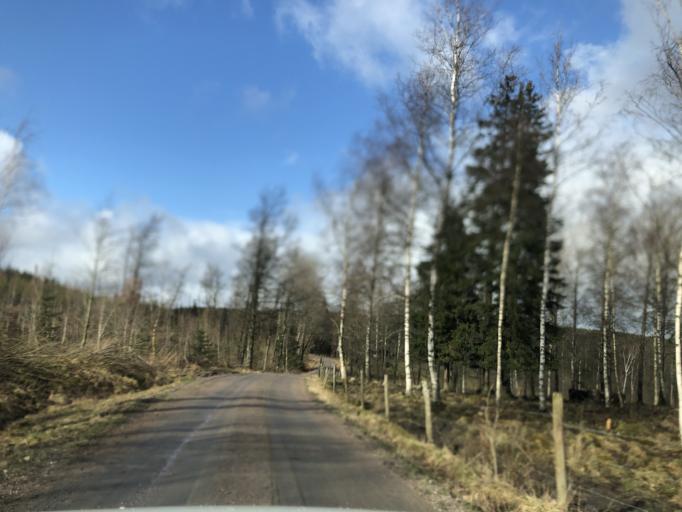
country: SE
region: Vaestra Goetaland
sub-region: Boras Kommun
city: Dalsjofors
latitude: 57.8253
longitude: 13.2058
